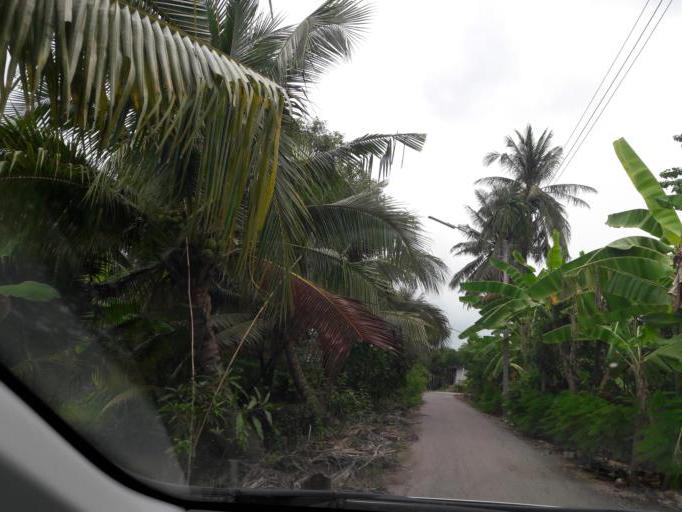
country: TH
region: Samut Sakhon
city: Ban Phaeo
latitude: 13.6138
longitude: 100.0243
